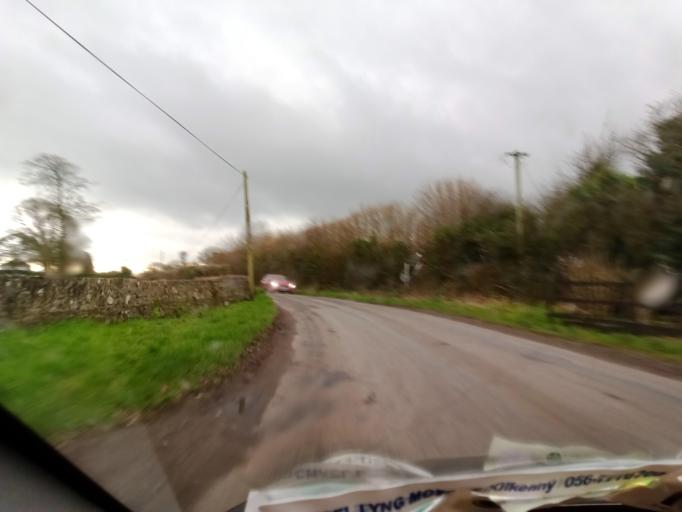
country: IE
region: Munster
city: Fethard
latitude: 52.5506
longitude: -7.7622
